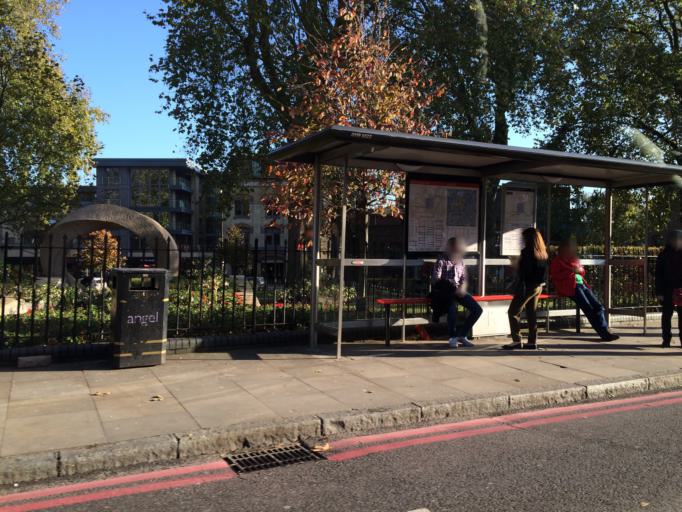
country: GB
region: England
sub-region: Greater London
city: Islington
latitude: 51.5363
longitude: -0.1035
